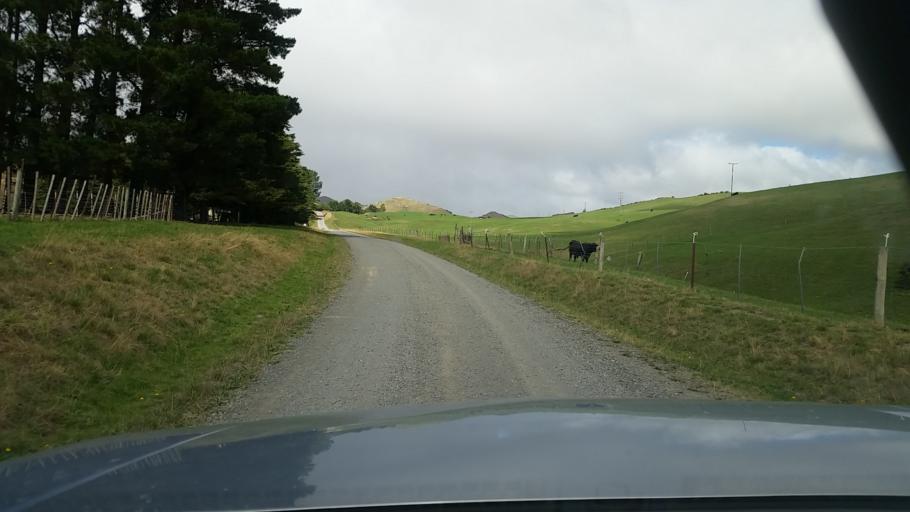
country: NZ
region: Marlborough
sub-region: Marlborough District
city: Blenheim
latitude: -41.7443
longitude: 173.8934
